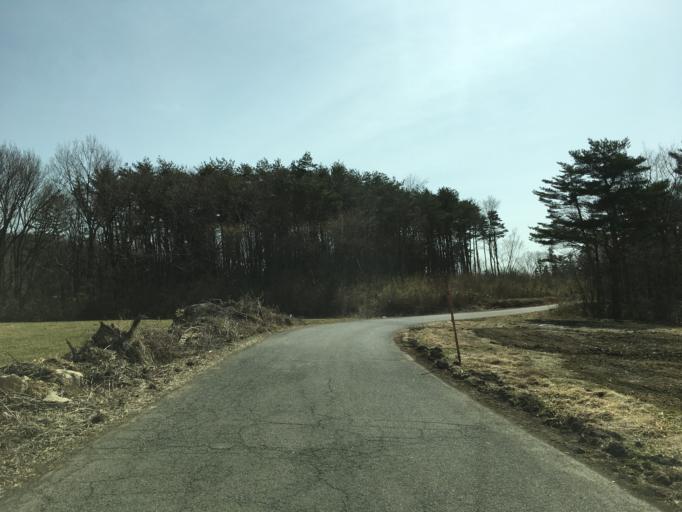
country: JP
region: Fukushima
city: Nihommatsu
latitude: 37.6258
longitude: 140.3603
